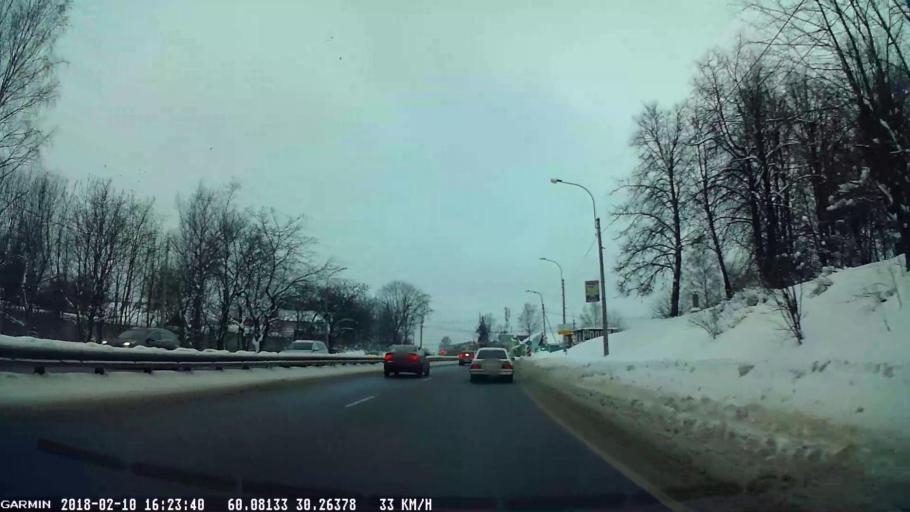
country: RU
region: St.-Petersburg
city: Pargolovo
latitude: 60.0813
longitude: 30.2631
